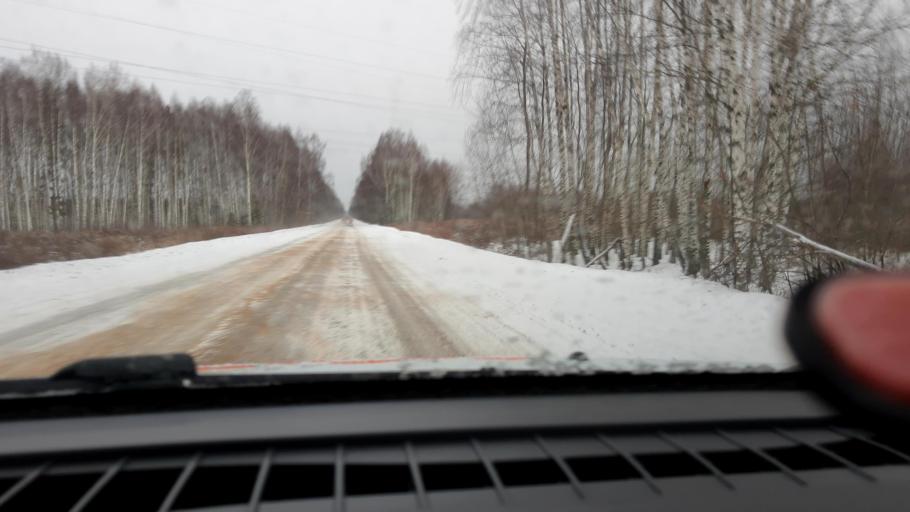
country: RU
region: Nizjnij Novgorod
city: Pamyat' Parizhskoy Kommuny
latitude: 56.2412
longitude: 44.5052
